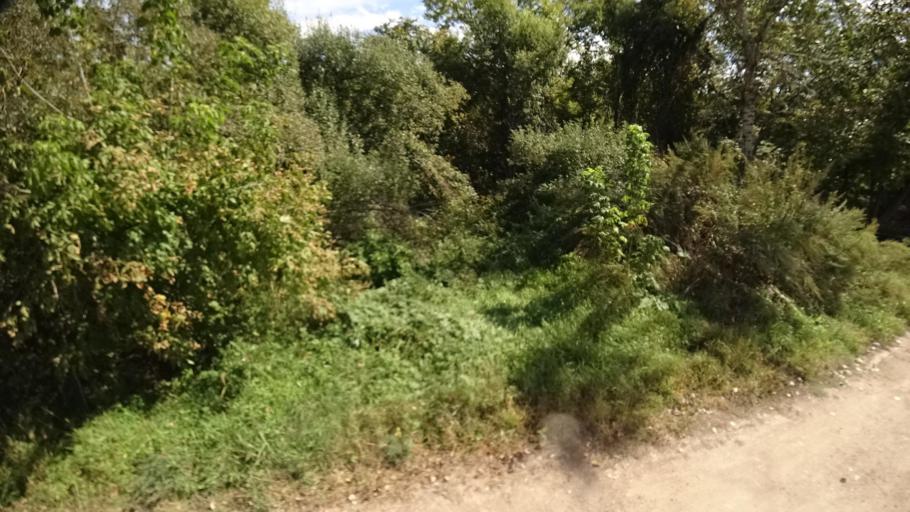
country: RU
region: Primorskiy
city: Yakovlevka
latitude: 44.4291
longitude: 133.5652
